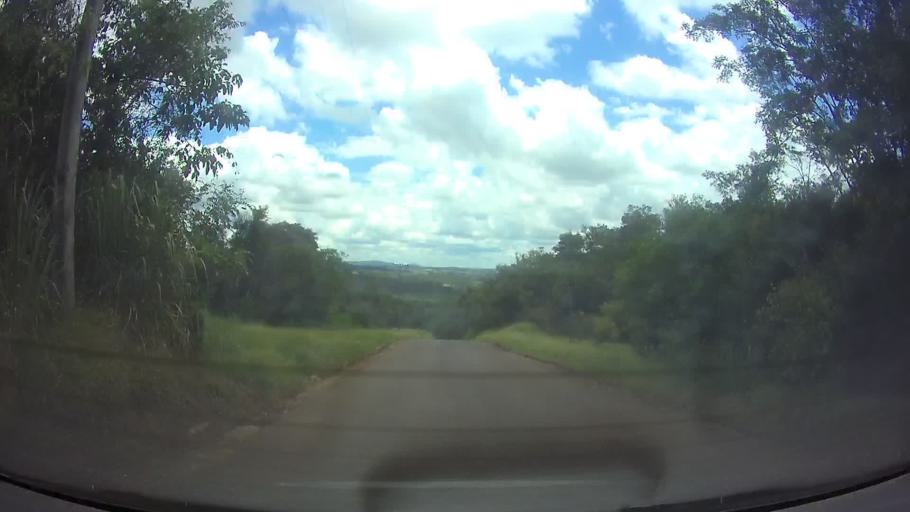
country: PY
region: Paraguari
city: La Colmena
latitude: -25.9281
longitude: -56.7881
